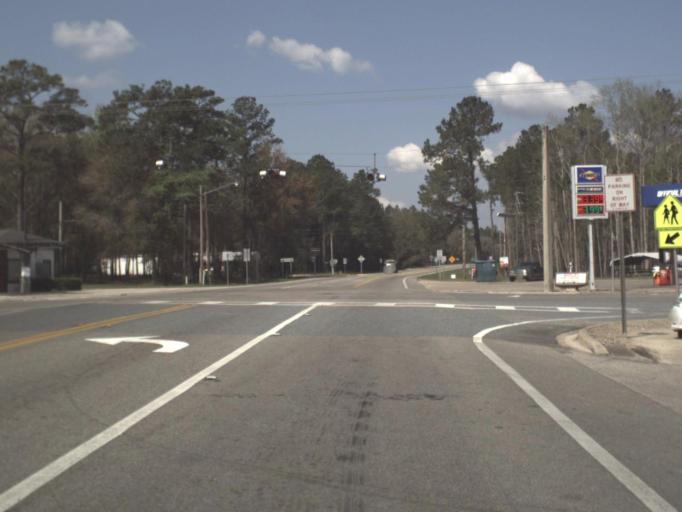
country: US
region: Florida
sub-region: Liberty County
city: Bristol
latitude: 30.3901
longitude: -84.7977
